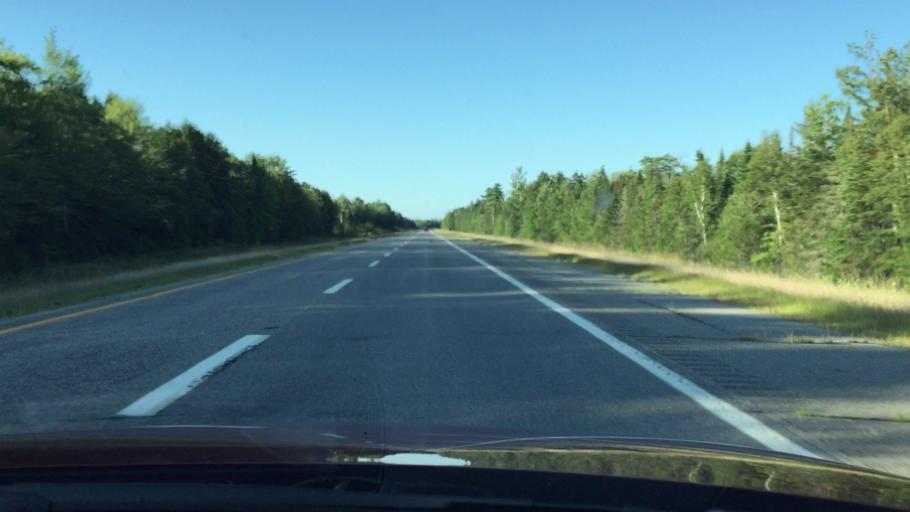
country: US
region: Maine
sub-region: Penobscot County
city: Howland
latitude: 45.2980
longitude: -68.6624
